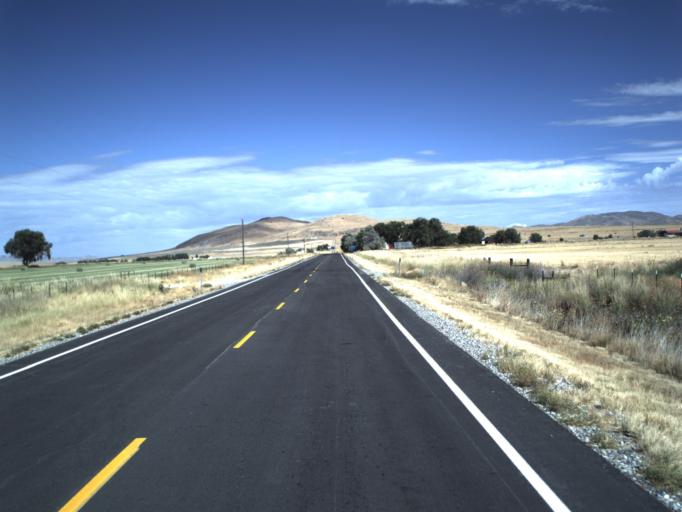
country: US
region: Utah
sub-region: Box Elder County
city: Garland
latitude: 41.7731
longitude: -112.4351
